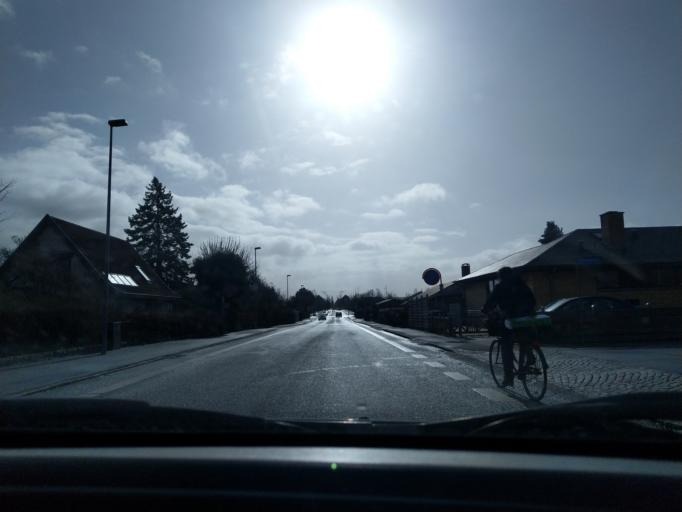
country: DK
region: Zealand
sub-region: Naestved Kommune
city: Naestved
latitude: 55.2179
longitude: 11.7683
